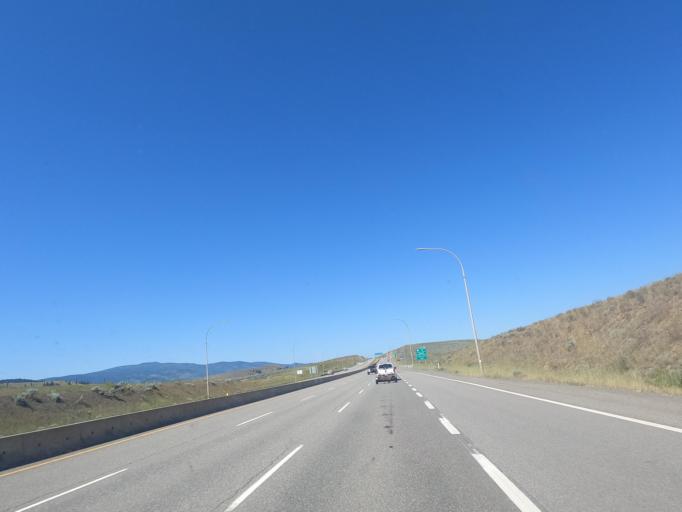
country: CA
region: British Columbia
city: Kamloops
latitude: 50.6651
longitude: -120.4385
